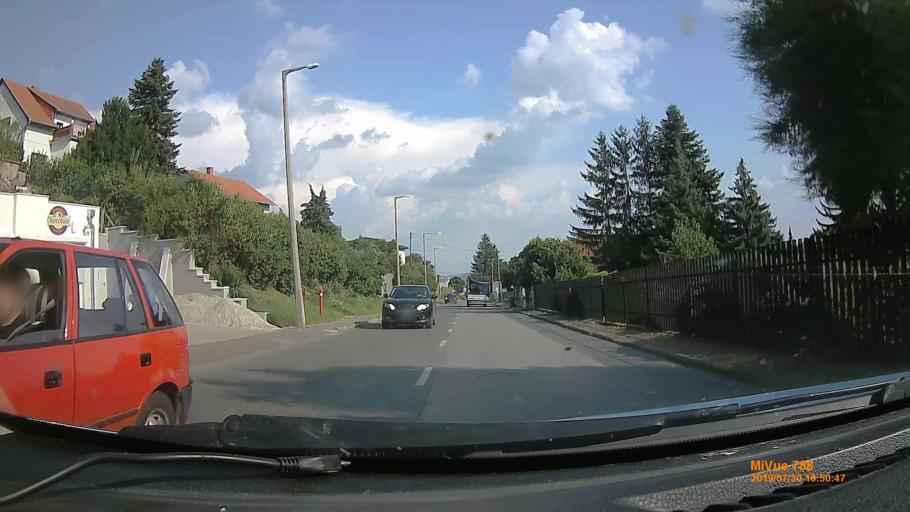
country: HU
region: Baranya
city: Pecs
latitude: 46.0814
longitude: 18.2093
